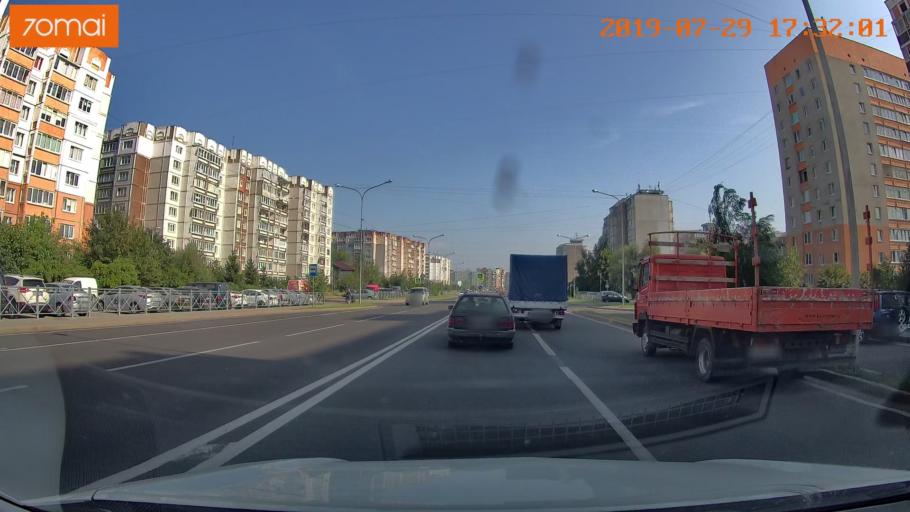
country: RU
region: Kaliningrad
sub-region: Gorod Kaliningrad
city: Kaliningrad
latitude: 54.7458
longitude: 20.4903
